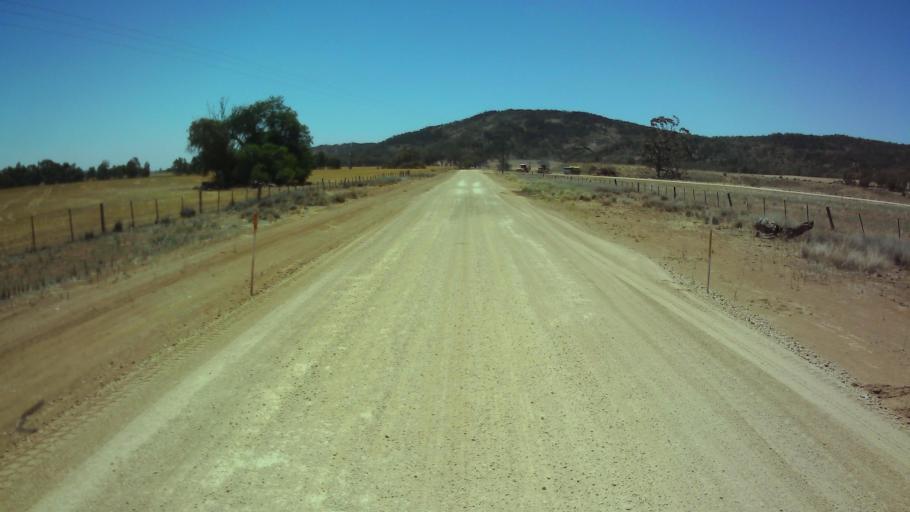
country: AU
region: New South Wales
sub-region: Weddin
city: Grenfell
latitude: -33.8583
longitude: 148.1073
